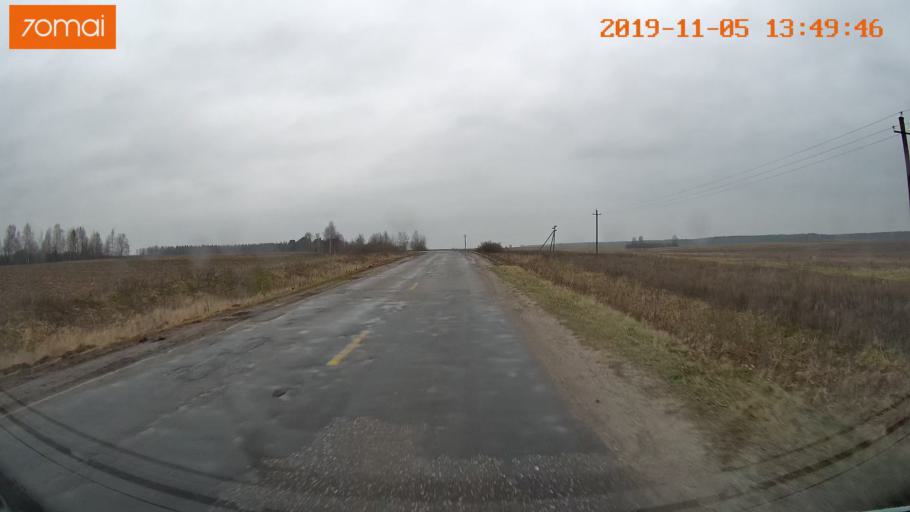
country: RU
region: Ivanovo
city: Kaminskiy
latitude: 57.0138
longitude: 41.4107
